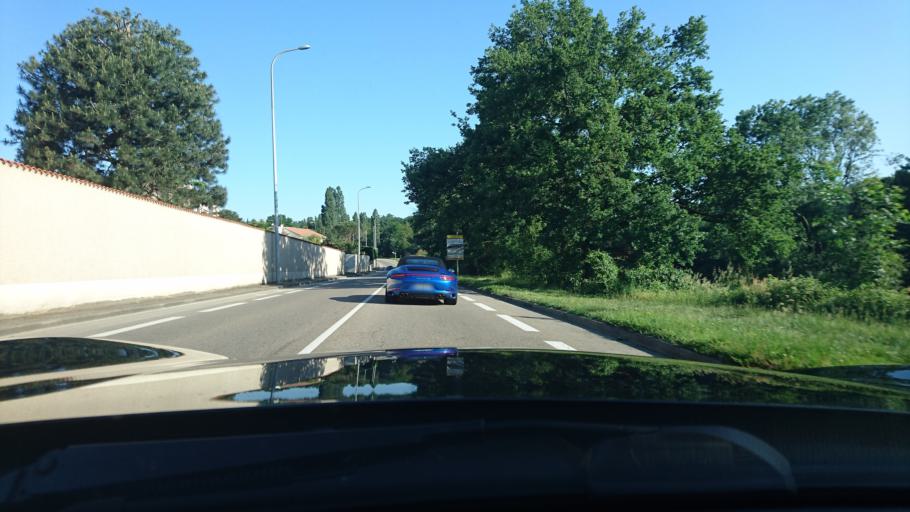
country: FR
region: Rhone-Alpes
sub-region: Departement du Rhone
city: Chaponost
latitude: 45.7028
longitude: 4.7537
